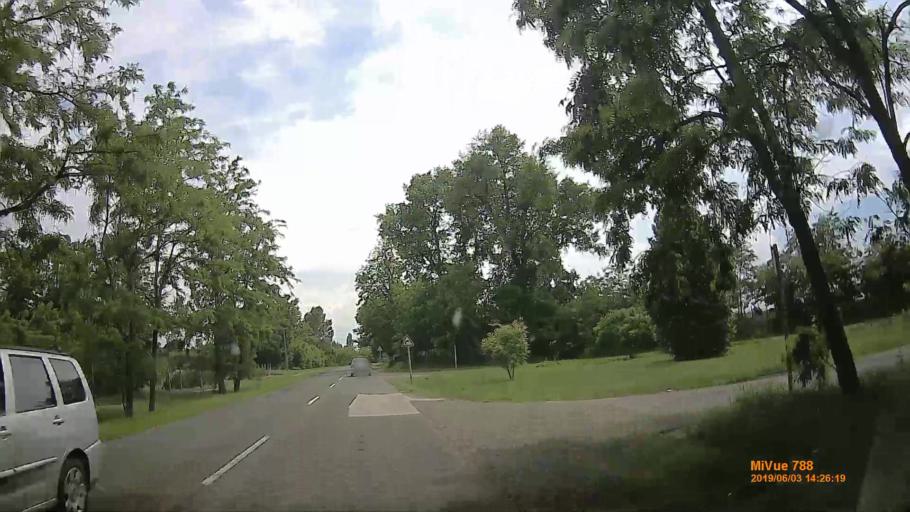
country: HU
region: Bacs-Kiskun
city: Tiszakecske
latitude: 46.9929
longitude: 20.1249
